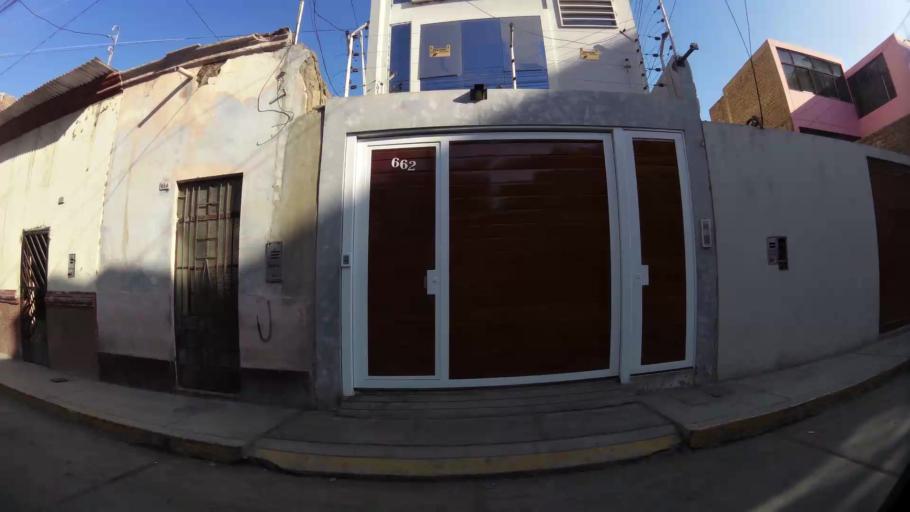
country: PE
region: Lambayeque
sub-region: Provincia de Chiclayo
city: Chiclayo
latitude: -6.7741
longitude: -79.8379
